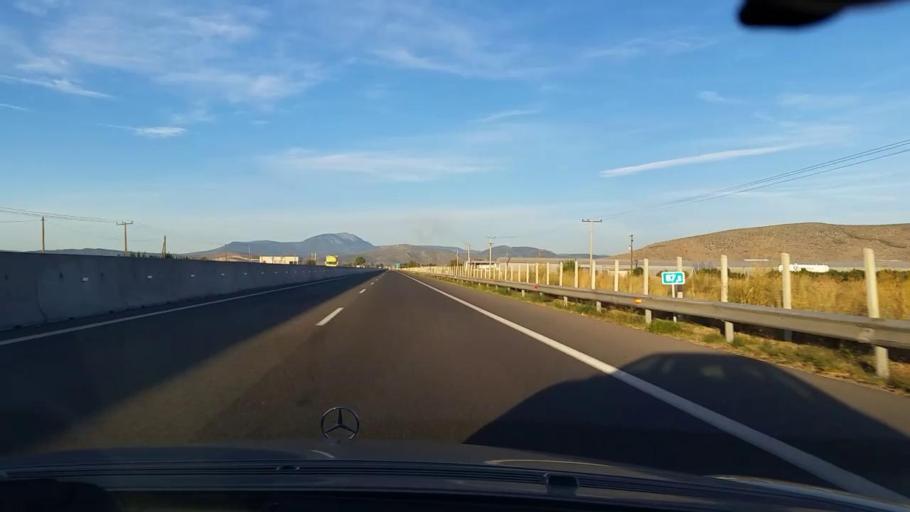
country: GR
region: Central Greece
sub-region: Nomos Voiotias
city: Thivai
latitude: 38.3676
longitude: 23.3503
